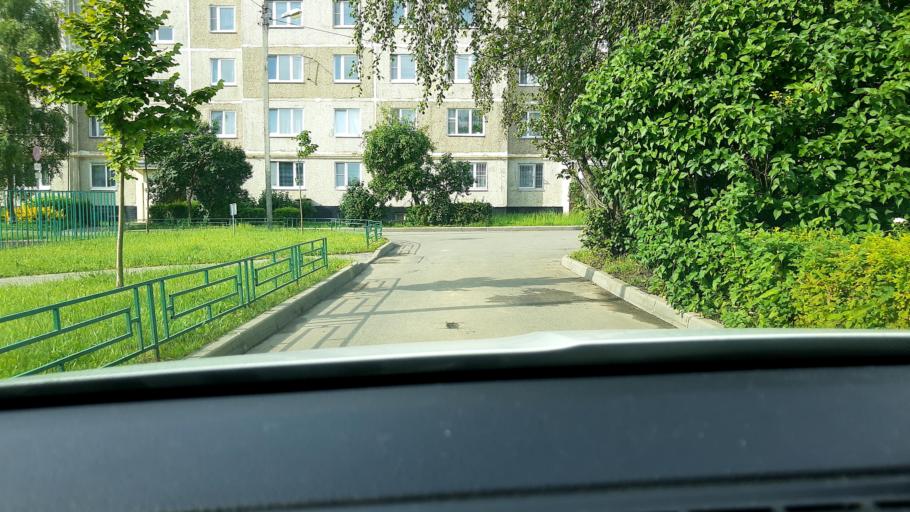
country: RU
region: Moskovskaya
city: Kokoshkino
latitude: 55.5372
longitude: 37.1610
